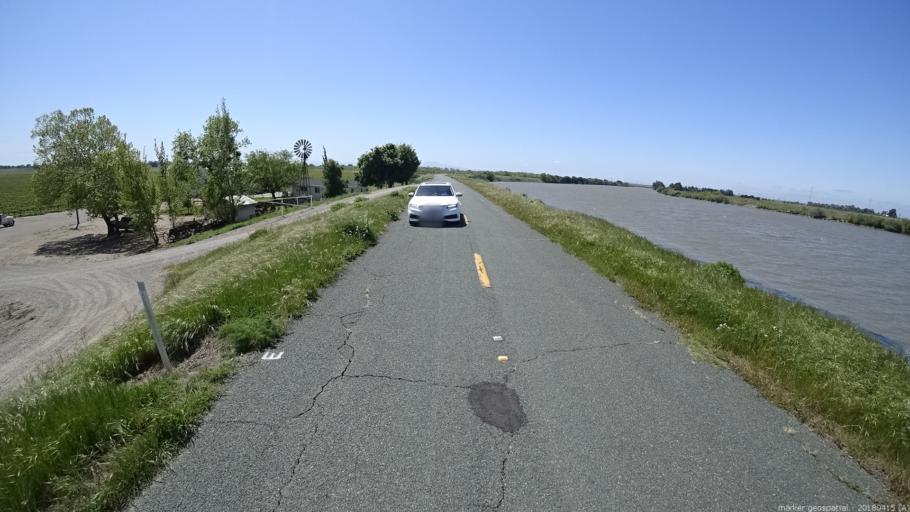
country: US
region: California
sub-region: Solano County
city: Rio Vista
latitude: 38.1873
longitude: -121.6428
